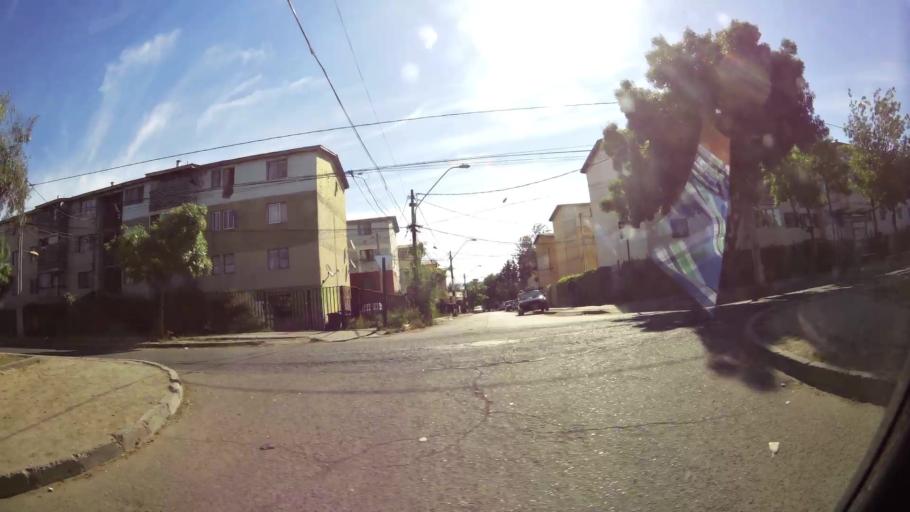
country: CL
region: Santiago Metropolitan
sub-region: Provincia de Santiago
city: Lo Prado
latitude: -33.4969
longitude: -70.7368
